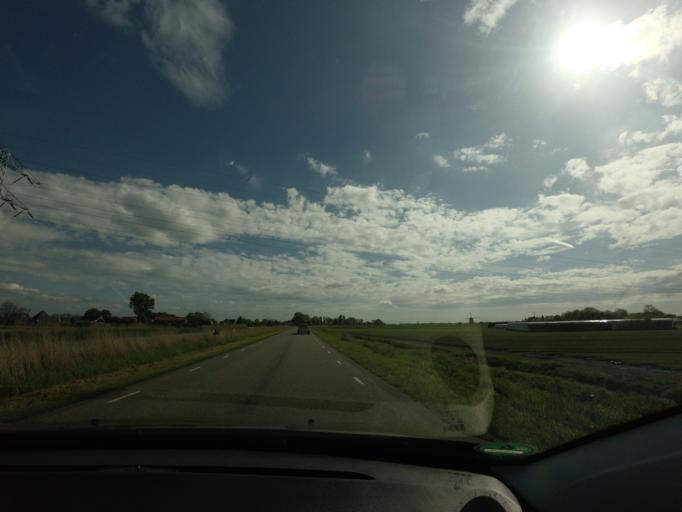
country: NL
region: North Holland
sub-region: Gemeente Heerhugowaard
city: Heerhugowaard
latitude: 52.6385
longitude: 4.8767
